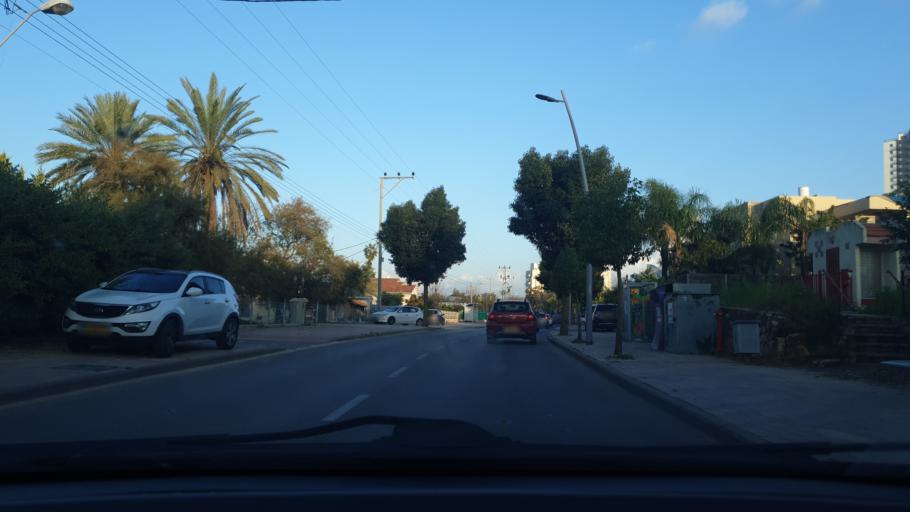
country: IL
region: Central District
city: Ramla
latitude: 31.9358
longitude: 34.8476
